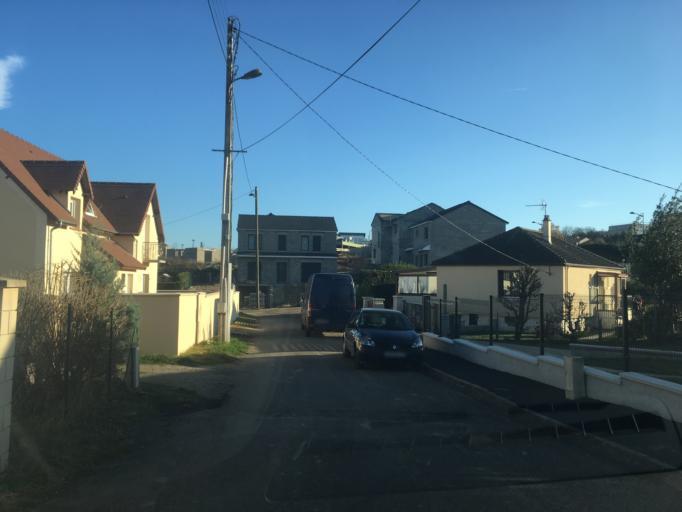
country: FR
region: Haute-Normandie
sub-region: Departement de l'Eure
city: Vernon
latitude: 49.0804
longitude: 1.4903
